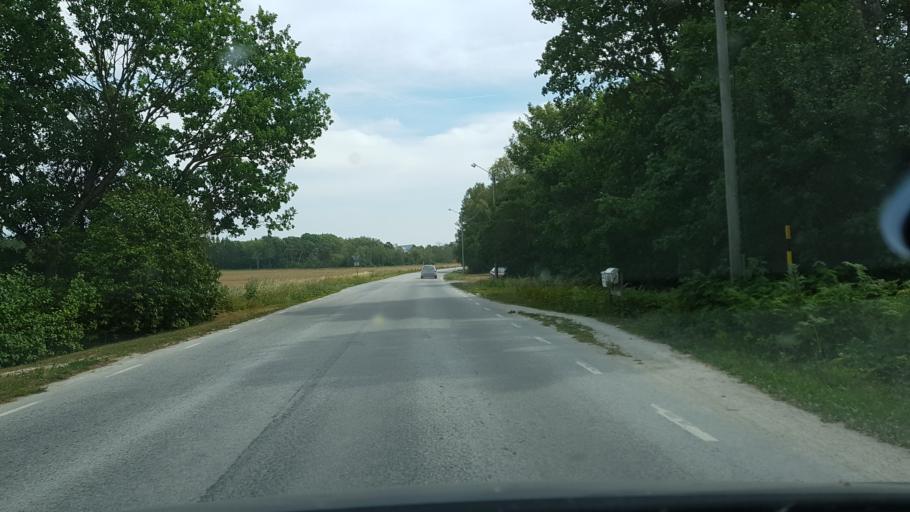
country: SE
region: Gotland
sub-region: Gotland
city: Slite
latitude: 57.7498
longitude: 18.7302
